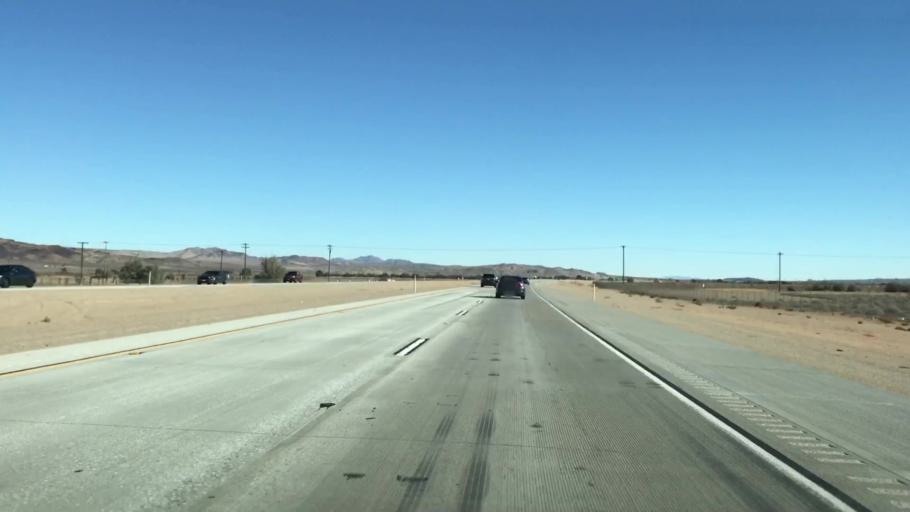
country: US
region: California
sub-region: San Bernardino County
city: Lenwood
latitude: 34.9171
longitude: -117.1747
